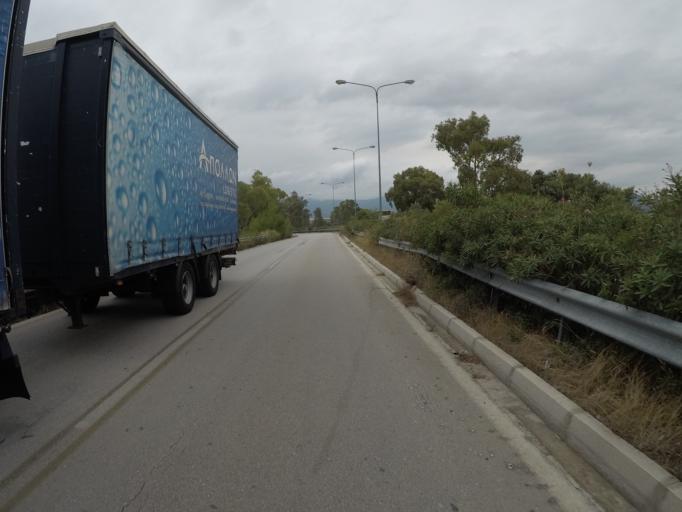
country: GR
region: Peloponnese
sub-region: Nomos Korinthias
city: Kyras Vrysi
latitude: 37.9298
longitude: 22.9944
